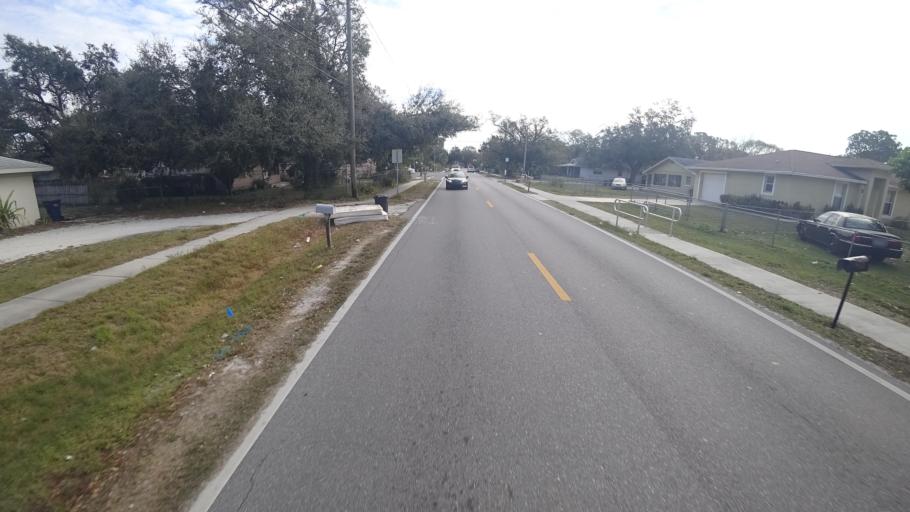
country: US
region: Florida
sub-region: Manatee County
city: West Samoset
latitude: 27.4734
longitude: -82.5594
